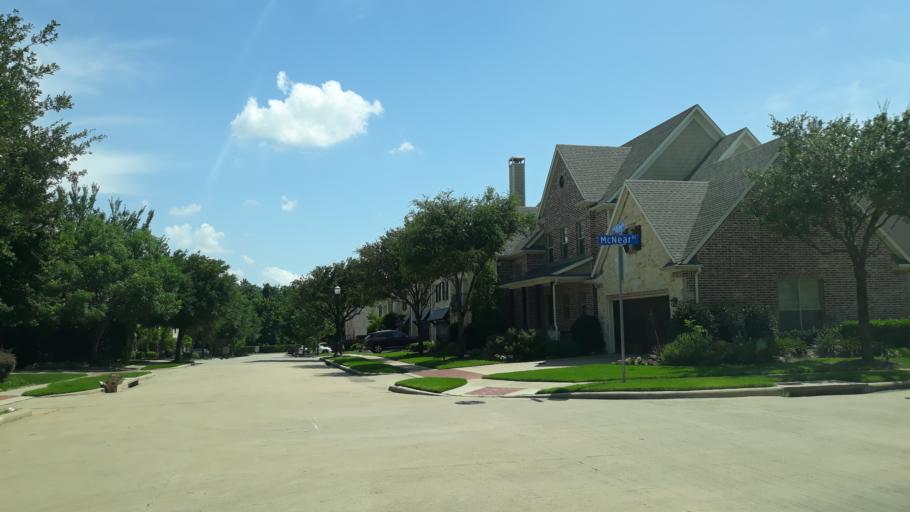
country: US
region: Texas
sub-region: Dallas County
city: Coppell
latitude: 32.9577
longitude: -97.0054
